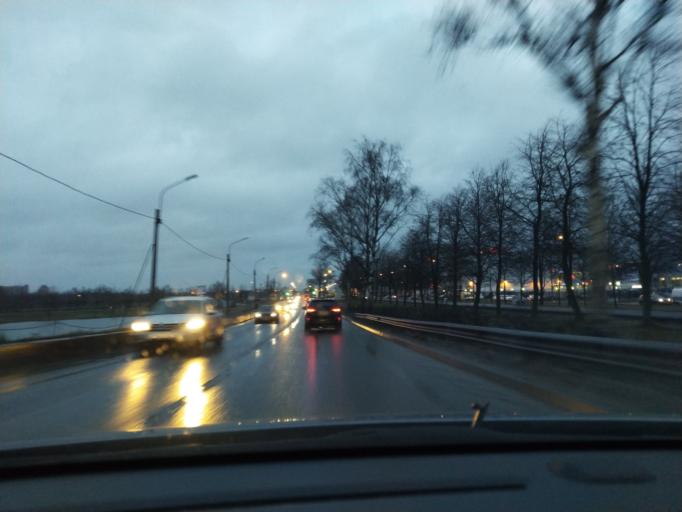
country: RU
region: St.-Petersburg
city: Uritsk
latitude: 59.8259
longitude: 30.1872
